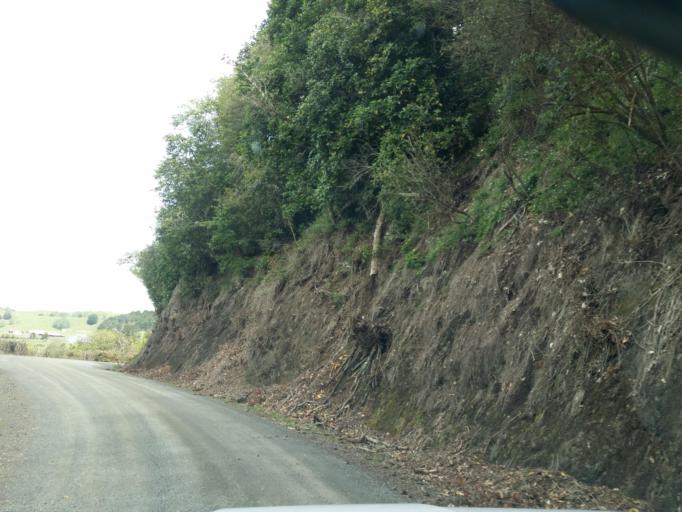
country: NZ
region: Northland
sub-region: Whangarei
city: Maungatapere
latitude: -35.8994
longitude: 174.0979
